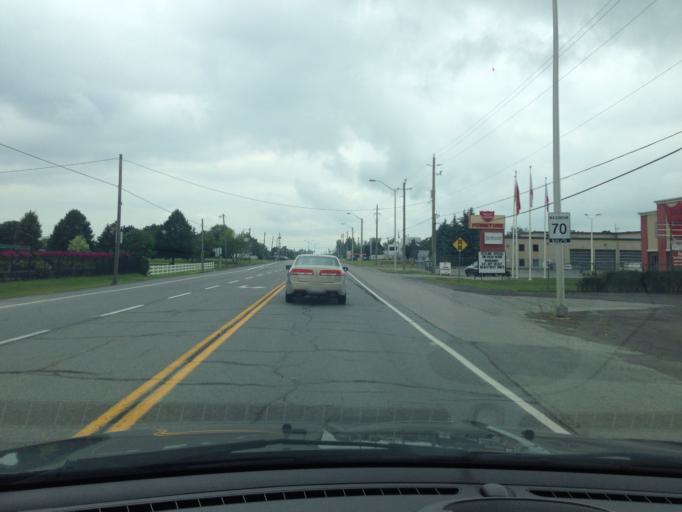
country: CA
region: Ontario
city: Ottawa
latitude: 45.3279
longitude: -75.5980
